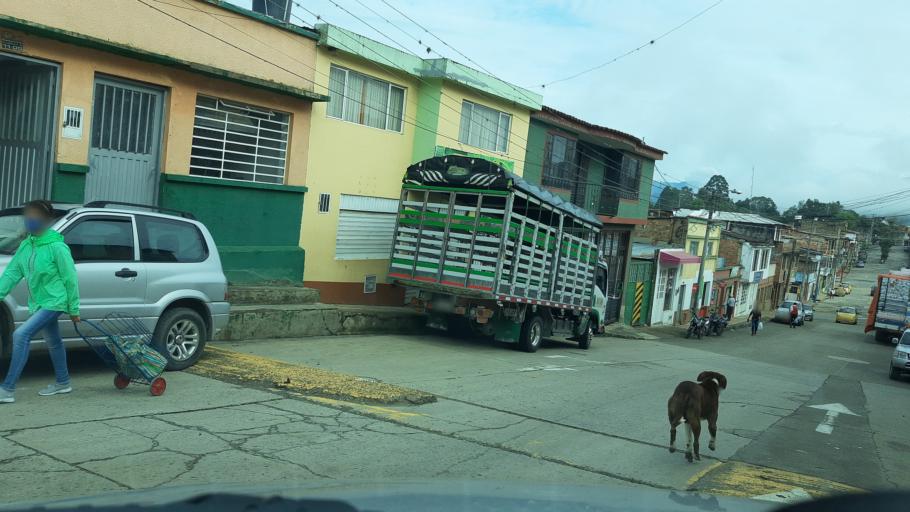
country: CO
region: Boyaca
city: Garagoa
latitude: 5.0832
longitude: -73.3656
